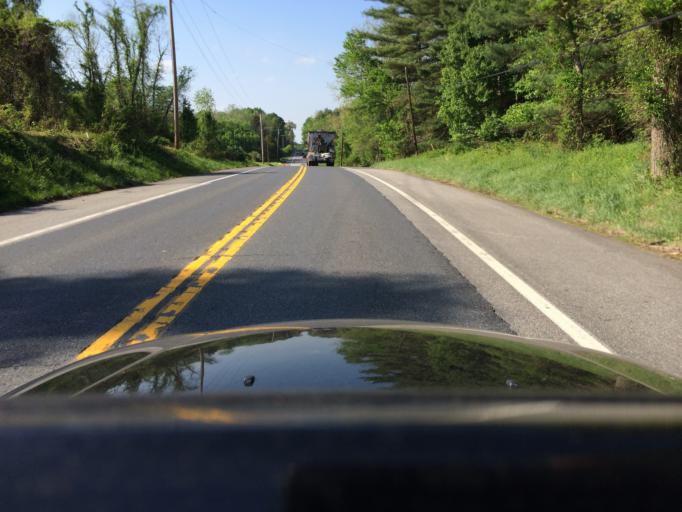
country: US
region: Maryland
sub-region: Montgomery County
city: Olney
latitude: 39.2437
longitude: -77.0546
